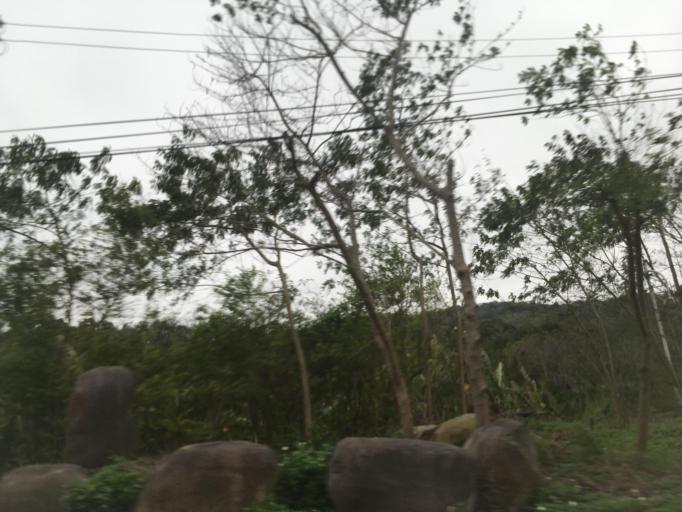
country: TW
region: Taiwan
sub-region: Miaoli
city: Miaoli
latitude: 24.4243
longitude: 120.7282
